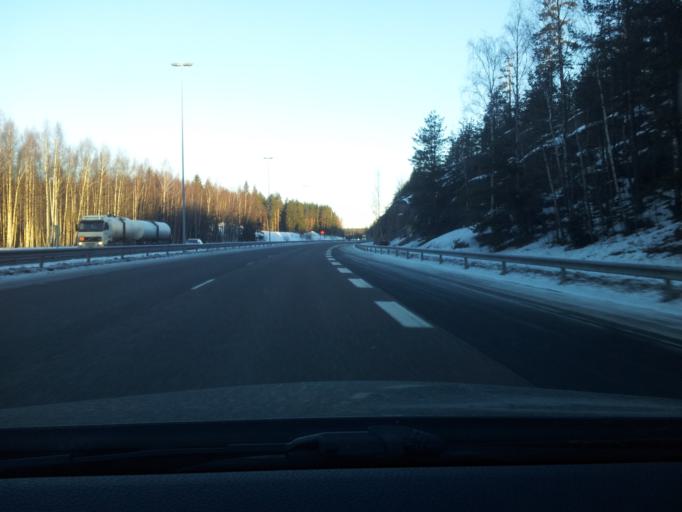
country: FI
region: Uusimaa
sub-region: Helsinki
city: Kirkkonummi
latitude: 60.2750
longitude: 24.4519
